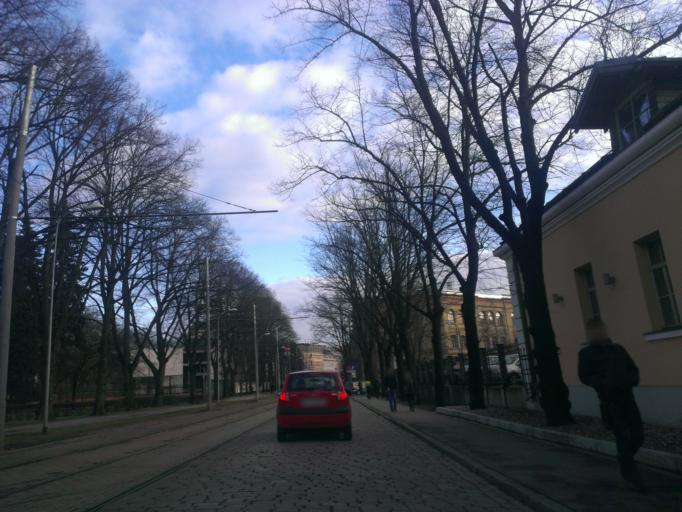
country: LV
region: Riga
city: Riga
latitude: 56.9552
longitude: 24.1027
